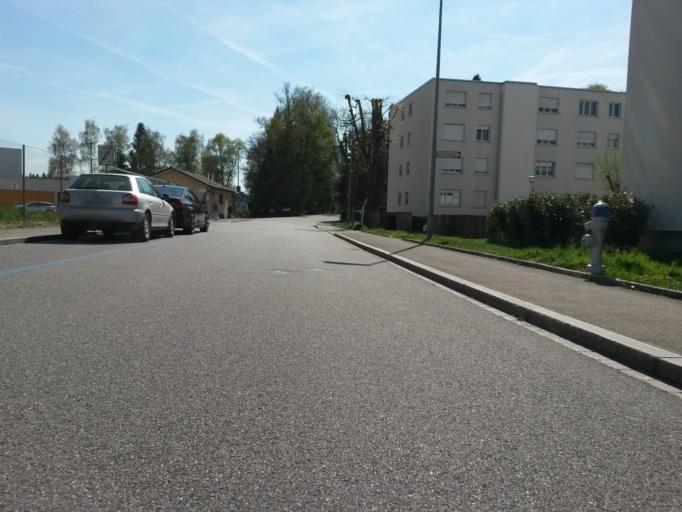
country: CH
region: Bern
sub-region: Oberaargau
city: Lotzwil
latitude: 47.2056
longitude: 7.7789
